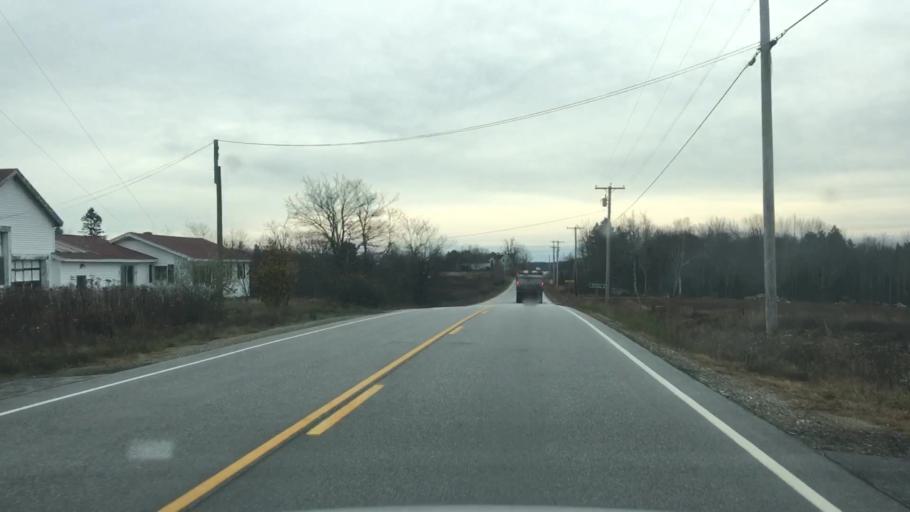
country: US
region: Maine
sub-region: Hancock County
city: Penobscot
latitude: 44.5251
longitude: -68.6643
